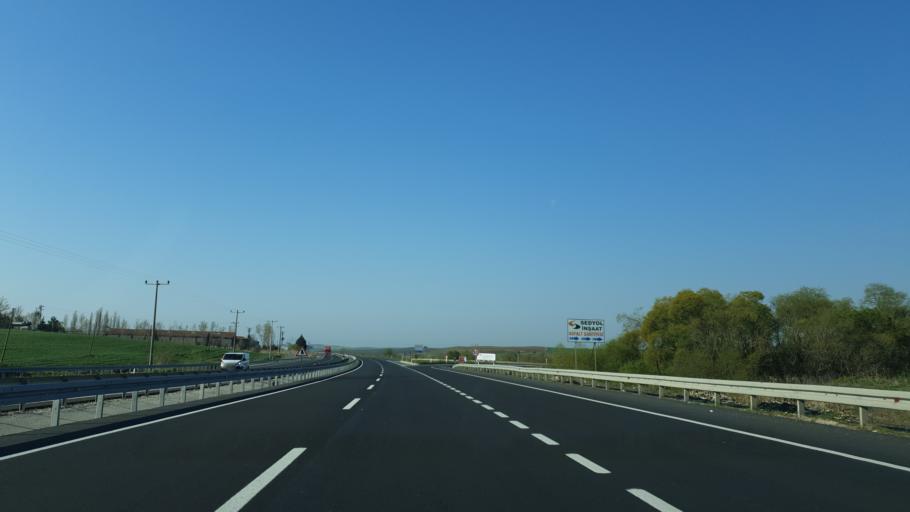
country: TR
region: Tekirdag
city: Corlu
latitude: 41.1228
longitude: 27.7526
